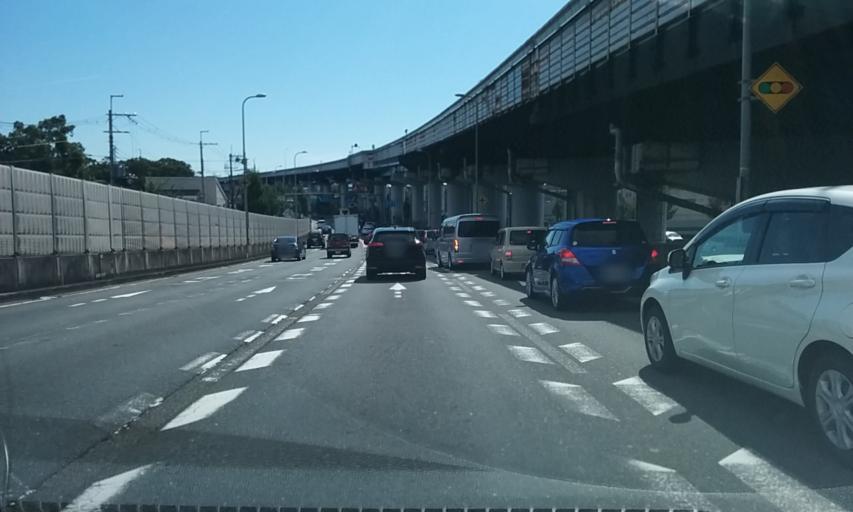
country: JP
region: Osaka
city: Ikeda
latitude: 34.8024
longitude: 135.4359
